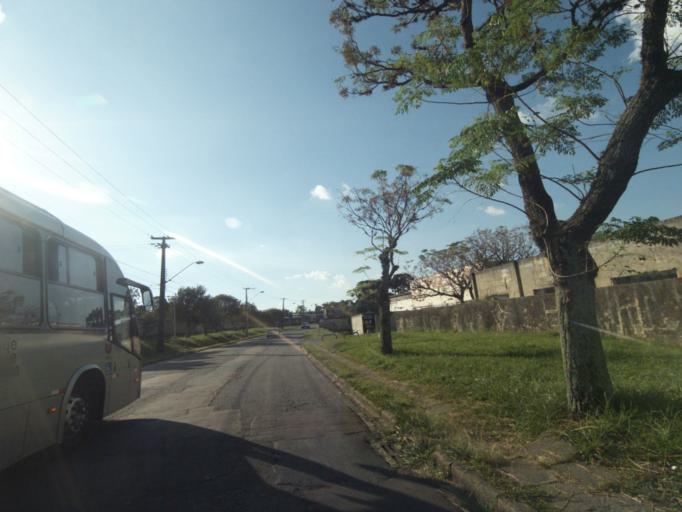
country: BR
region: Parana
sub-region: Curitiba
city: Curitiba
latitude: -25.4610
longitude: -49.2549
